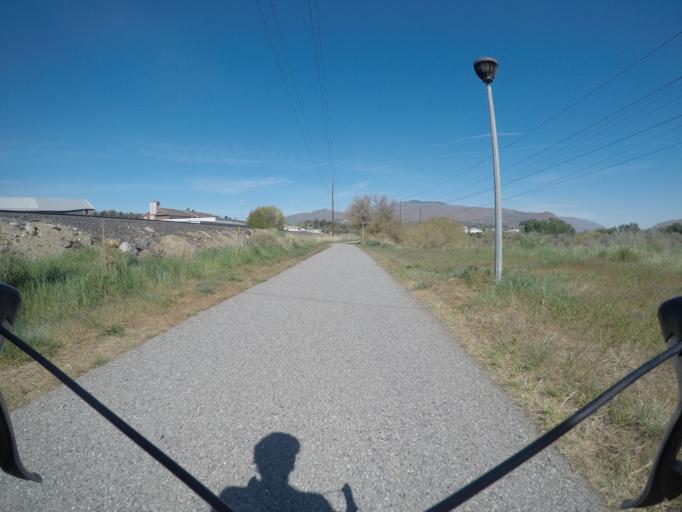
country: US
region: Washington
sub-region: Chelan County
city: Sunnyslope
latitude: 47.4520
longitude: -120.3309
